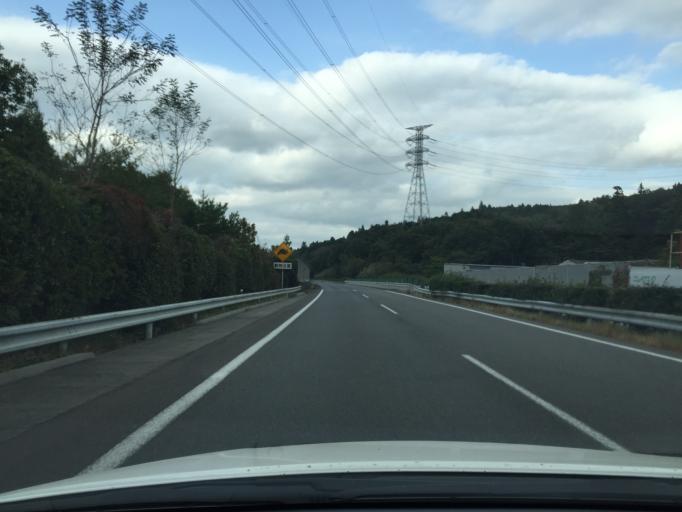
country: JP
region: Ibaraki
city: Kitaibaraki
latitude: 36.9361
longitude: 140.7706
